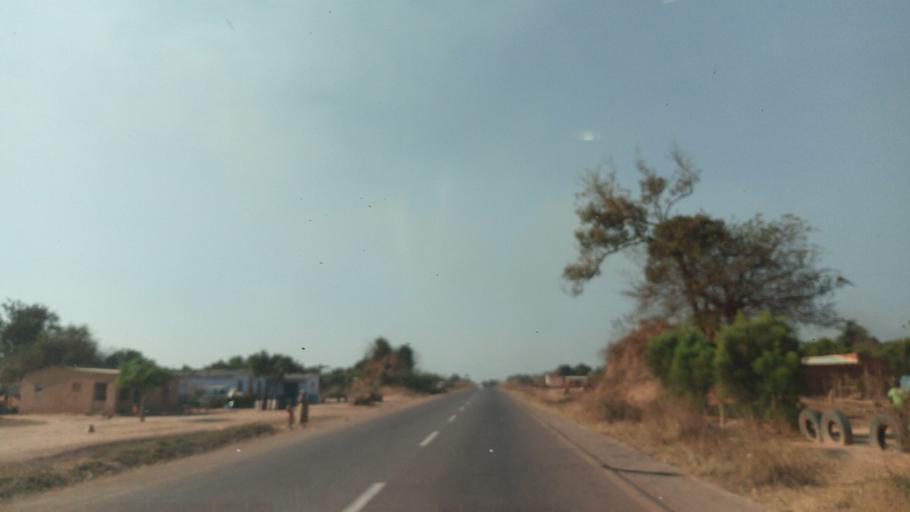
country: CD
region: Katanga
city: Lubumbashi
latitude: -11.4290
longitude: 27.7244
